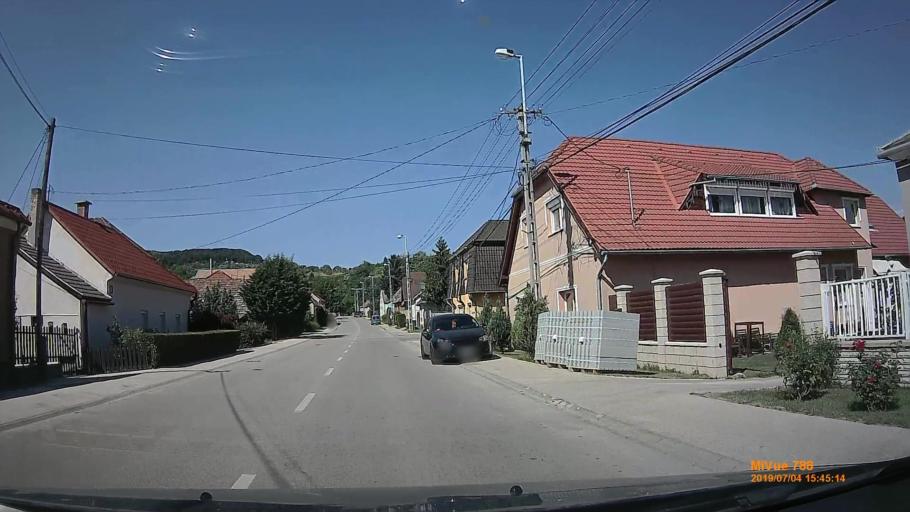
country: HU
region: Komarom-Esztergom
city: Tatabanya
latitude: 47.5707
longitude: 18.4154
